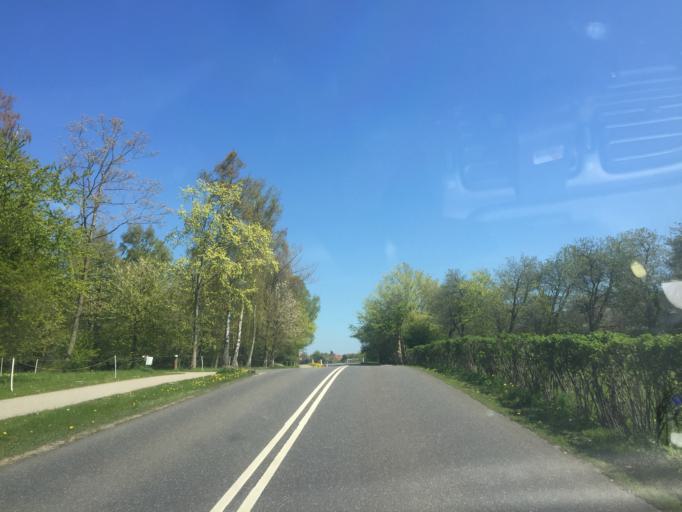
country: DK
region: Capital Region
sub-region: Egedal Kommune
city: Ganlose
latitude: 55.7848
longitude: 12.2516
